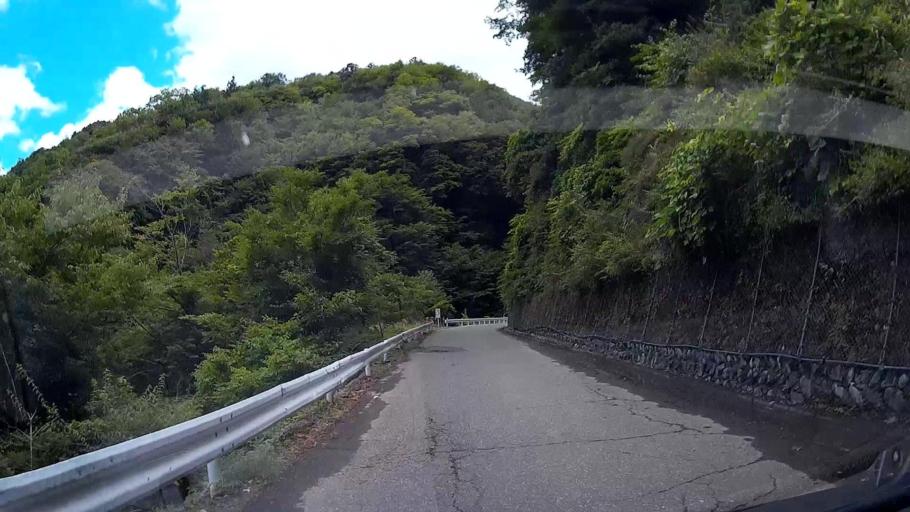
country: JP
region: Shizuoka
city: Shizuoka-shi
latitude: 35.3192
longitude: 138.1822
